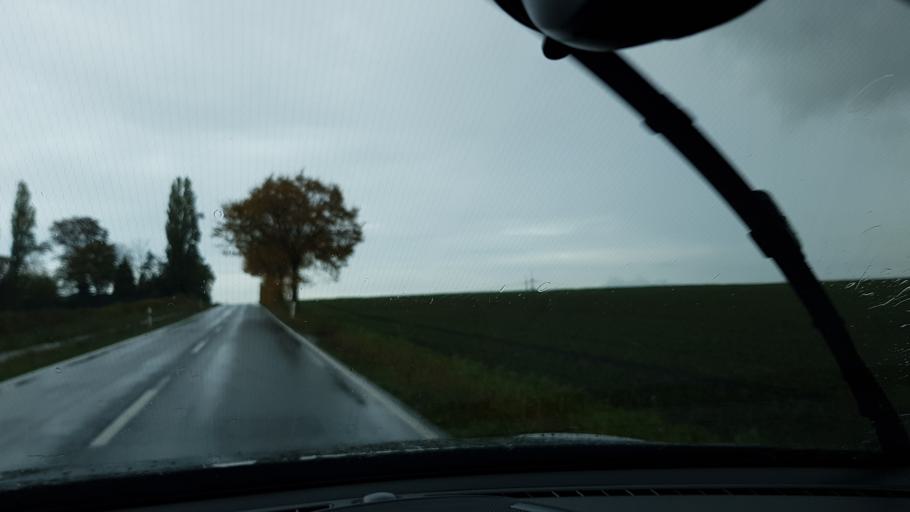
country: DE
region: North Rhine-Westphalia
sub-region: Regierungsbezirk Dusseldorf
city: Rommerskirchen
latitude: 51.0420
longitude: 6.6274
